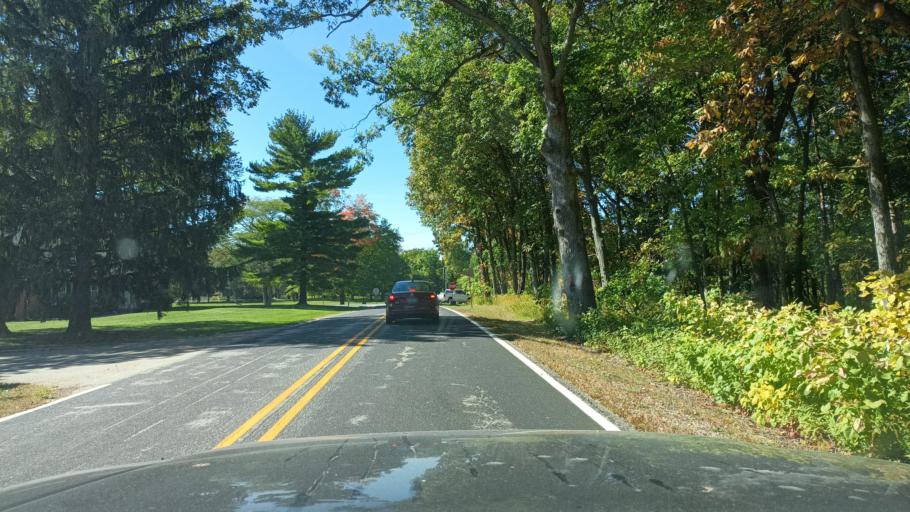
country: US
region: Illinois
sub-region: Champaign County
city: Lake of the Woods
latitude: 40.2077
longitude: -88.3689
